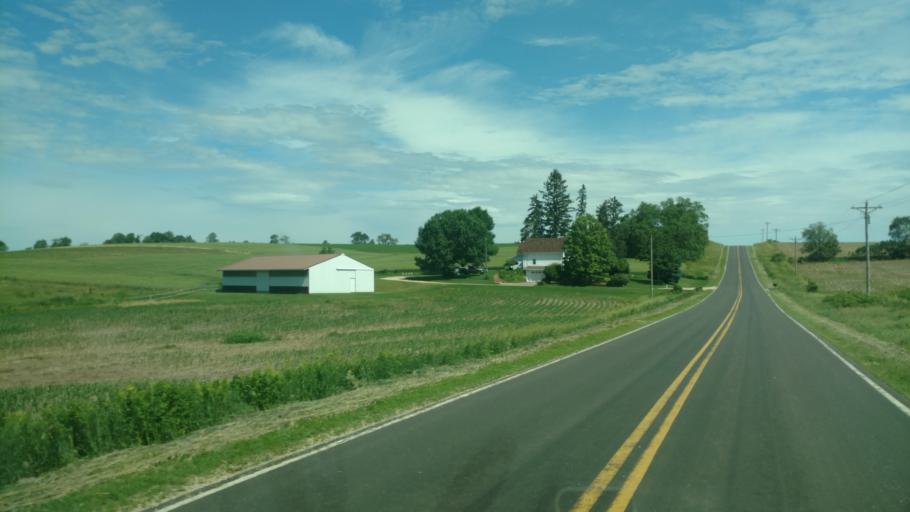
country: US
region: Wisconsin
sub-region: Vernon County
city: Hillsboro
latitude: 43.7136
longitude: -90.4477
